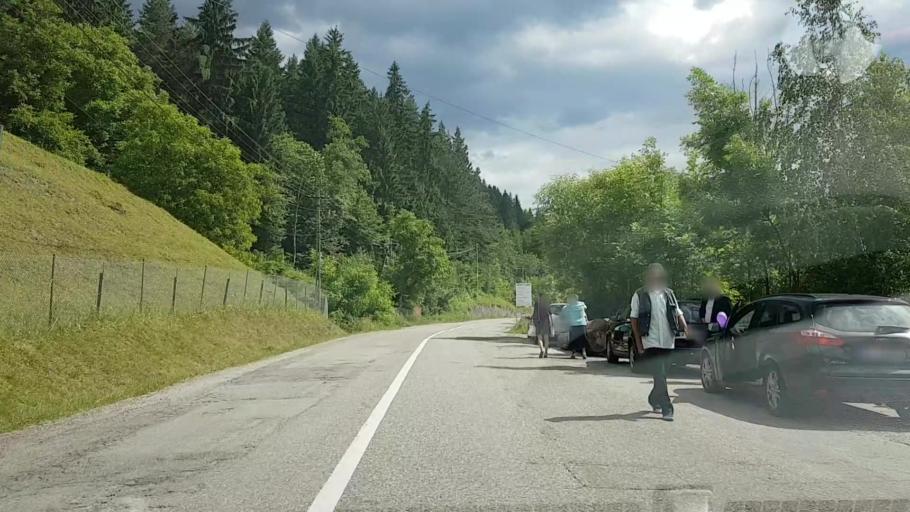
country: RO
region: Neamt
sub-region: Comuna Poiana Teiului
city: Poiana Teiului
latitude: 47.0880
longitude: 25.9703
